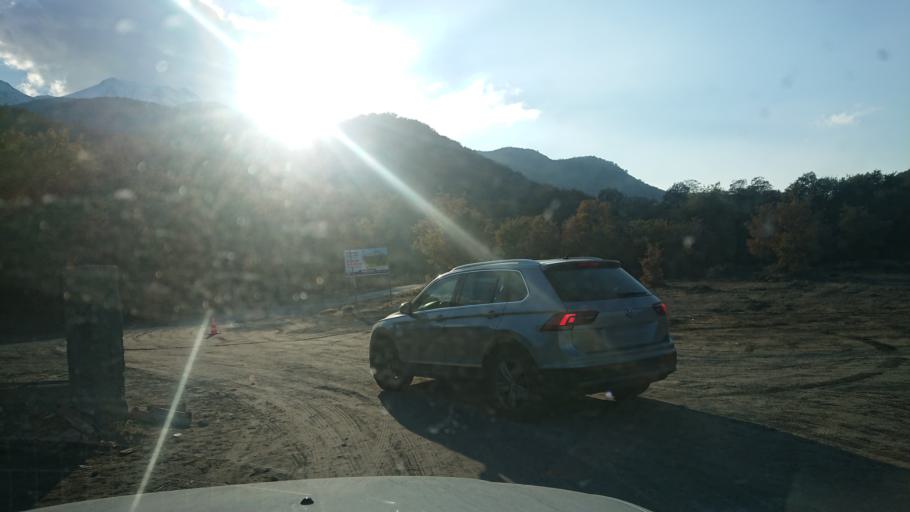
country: TR
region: Aksaray
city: Taspinar
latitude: 38.1661
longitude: 34.2028
